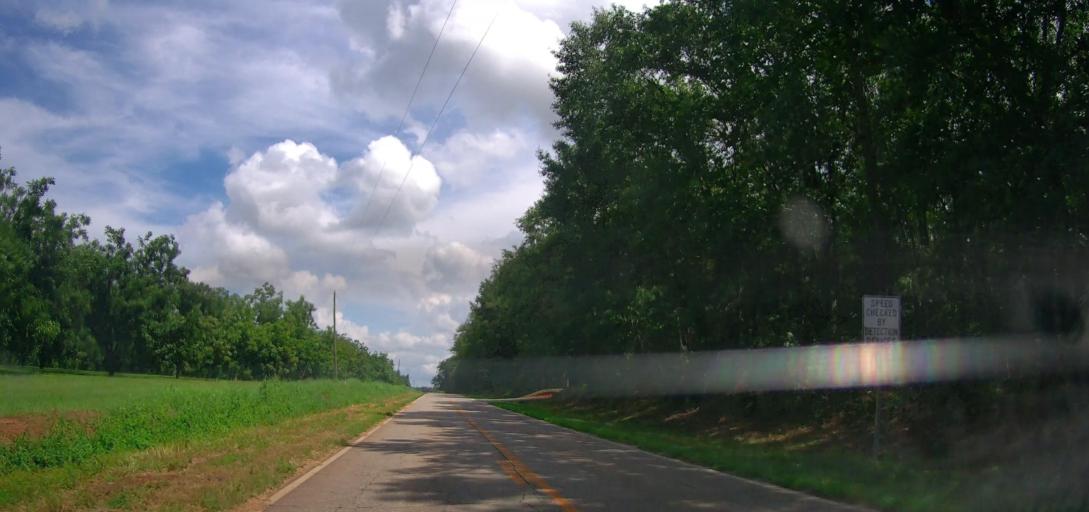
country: US
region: Georgia
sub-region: Houston County
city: Perry
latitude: 32.5212
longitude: -83.7768
